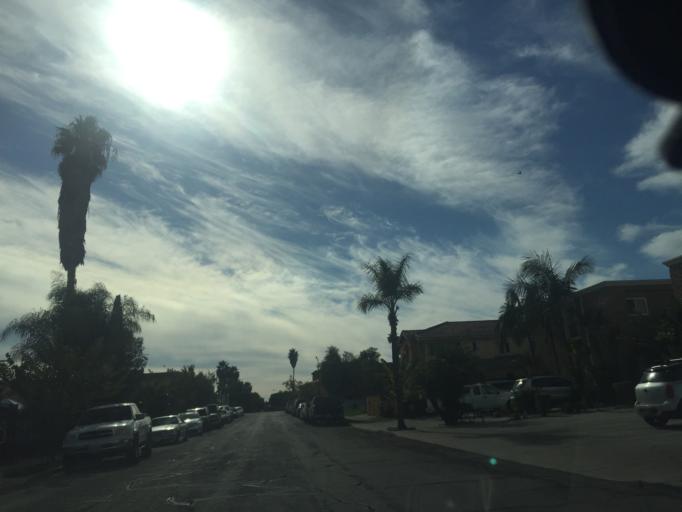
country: US
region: California
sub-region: San Diego County
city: Lemon Grove
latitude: 32.7508
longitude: -117.0955
